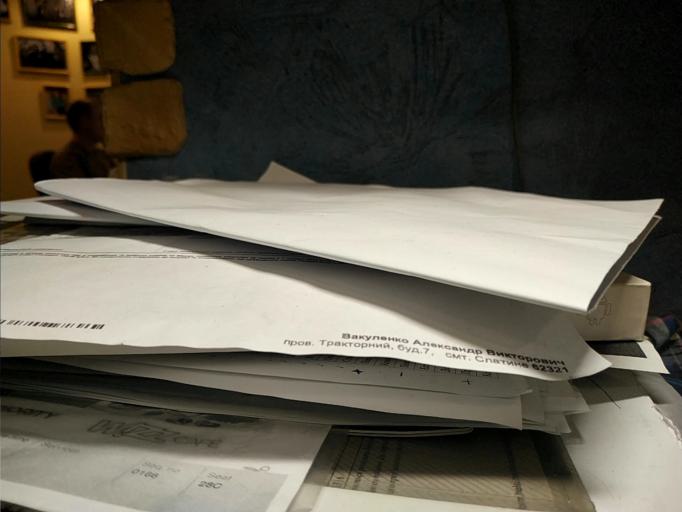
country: RU
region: Tverskaya
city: Zubtsov
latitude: 56.1206
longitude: 34.5711
